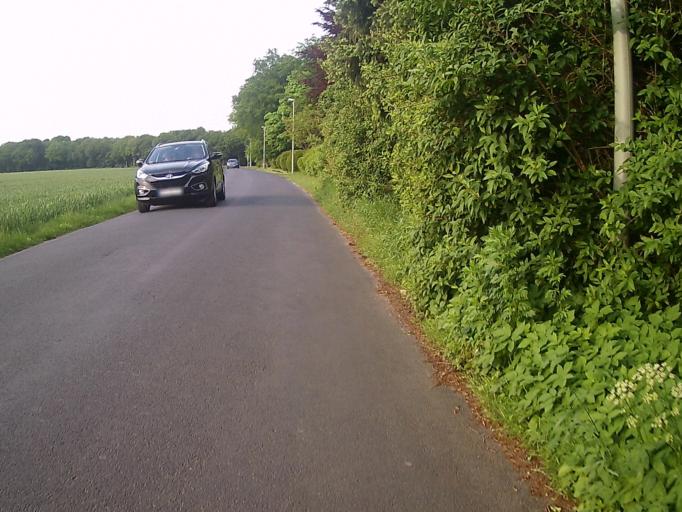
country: DE
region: North Rhine-Westphalia
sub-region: Regierungsbezirk Dusseldorf
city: Krefeld
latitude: 51.3980
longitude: 6.5301
